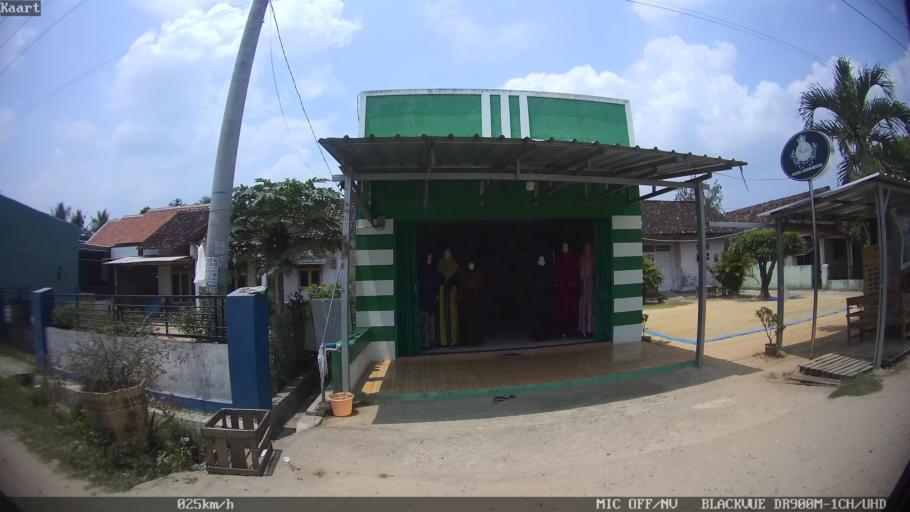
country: ID
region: Lampung
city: Pringsewu
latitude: -5.3486
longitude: 104.9852
